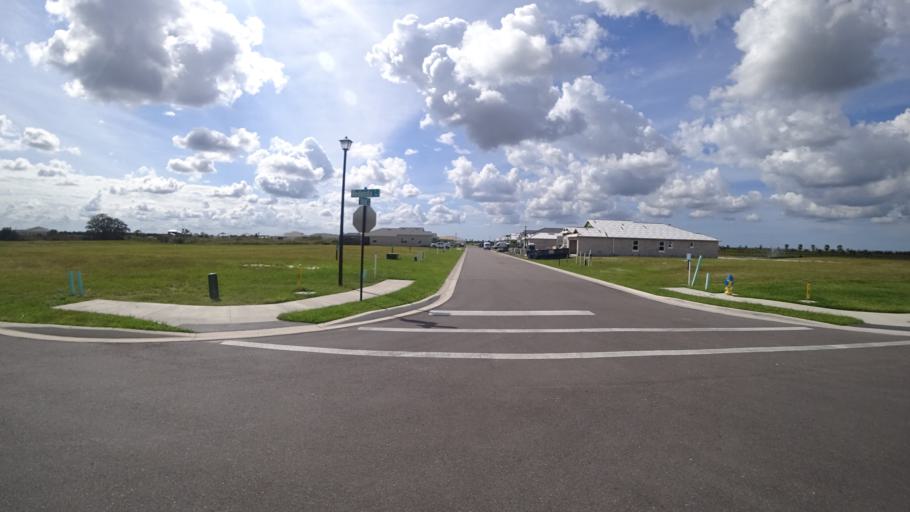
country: US
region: Florida
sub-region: Sarasota County
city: The Meadows
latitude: 27.3987
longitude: -82.3595
